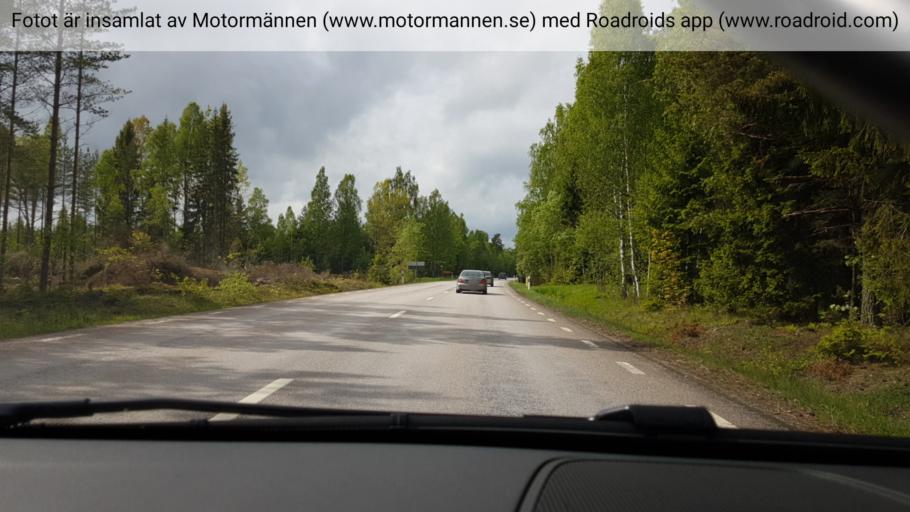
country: SE
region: Uppsala
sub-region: Osthammars Kommun
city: Osterbybruk
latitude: 60.1737
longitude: 17.9235
